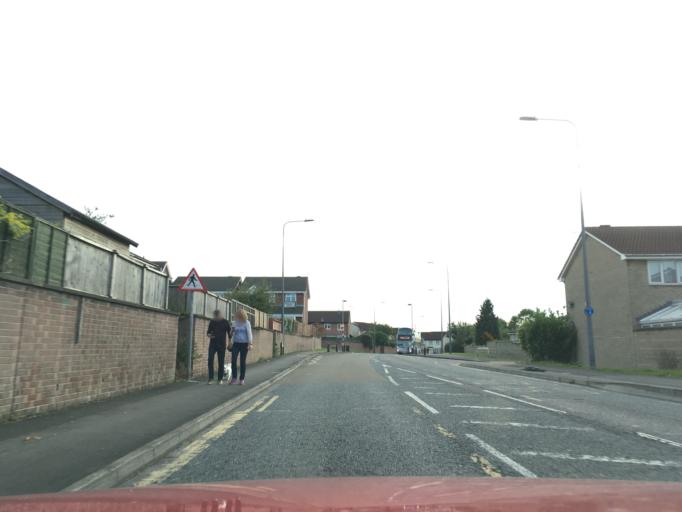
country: GB
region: England
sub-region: South Gloucestershire
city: Stoke Gifford
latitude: 51.5247
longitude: -2.5345
